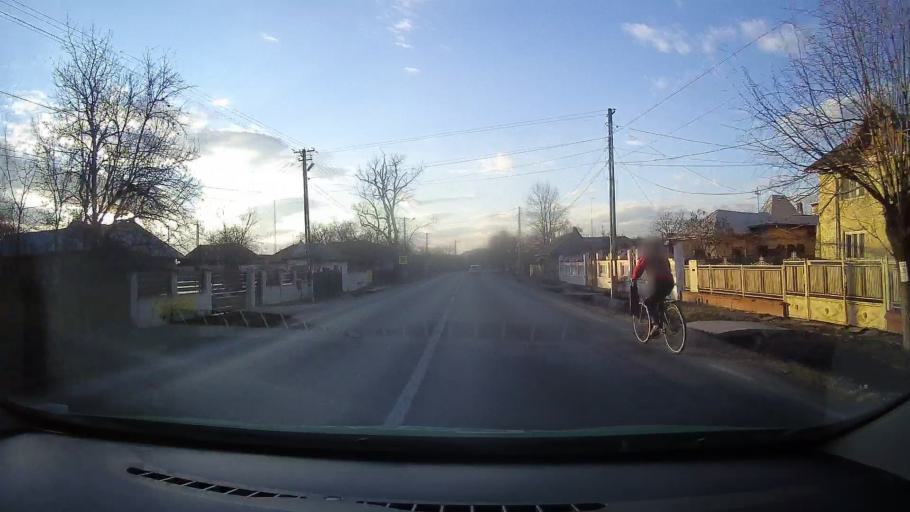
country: RO
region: Dambovita
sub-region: Comuna Gura Ocnitei
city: Adanca
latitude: 44.9076
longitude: 25.6218
